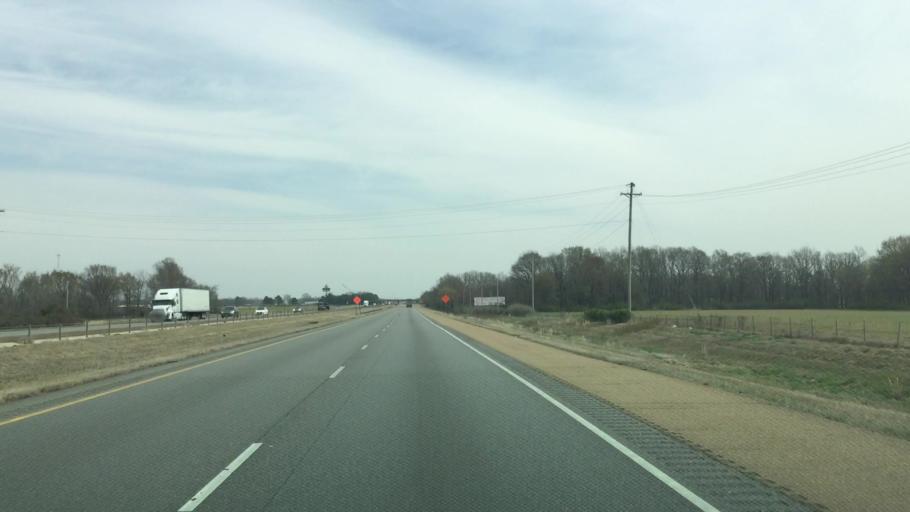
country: US
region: Arkansas
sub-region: Saint Francis County
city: Forrest City
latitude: 34.9782
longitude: -90.9177
